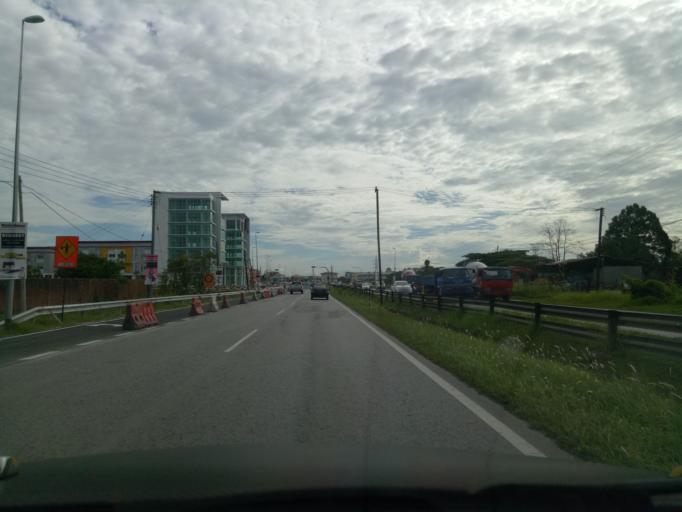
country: MY
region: Sarawak
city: Kuching
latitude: 1.4626
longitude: 110.3270
